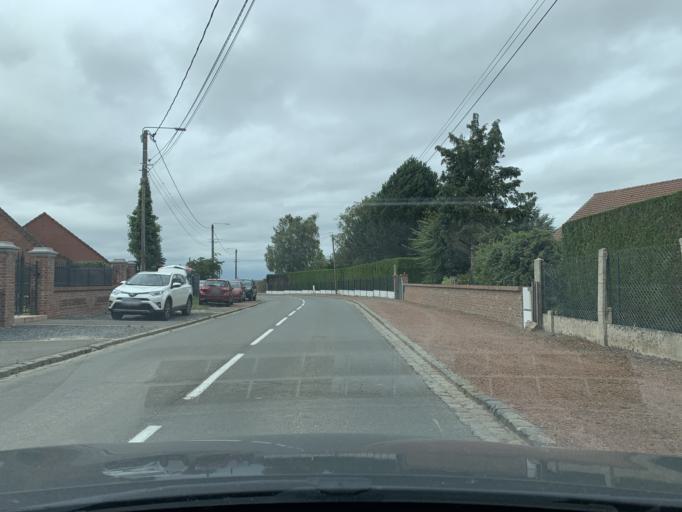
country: FR
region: Nord-Pas-de-Calais
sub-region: Departement du Nord
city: Fechain
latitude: 50.2374
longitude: 3.2093
